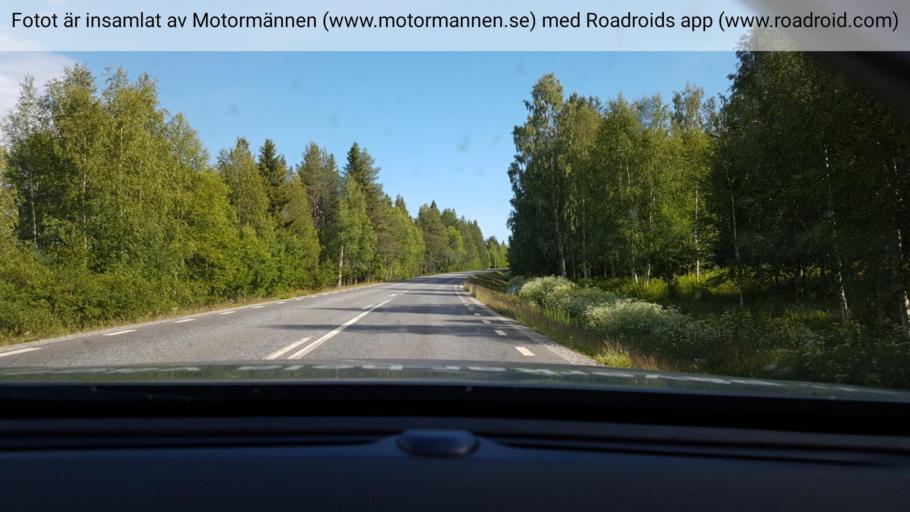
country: SE
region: Vaesterbotten
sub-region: Lycksele Kommun
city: Soderfors
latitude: 64.8165
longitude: 18.0708
